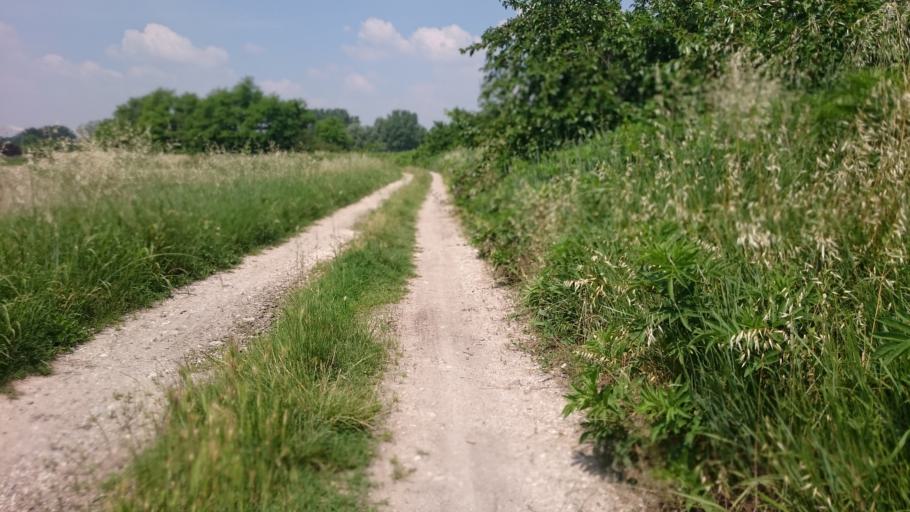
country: IT
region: Lombardy
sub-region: Provincia di Mantova
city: Lunetta-Frassino
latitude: 45.1276
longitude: 10.8262
